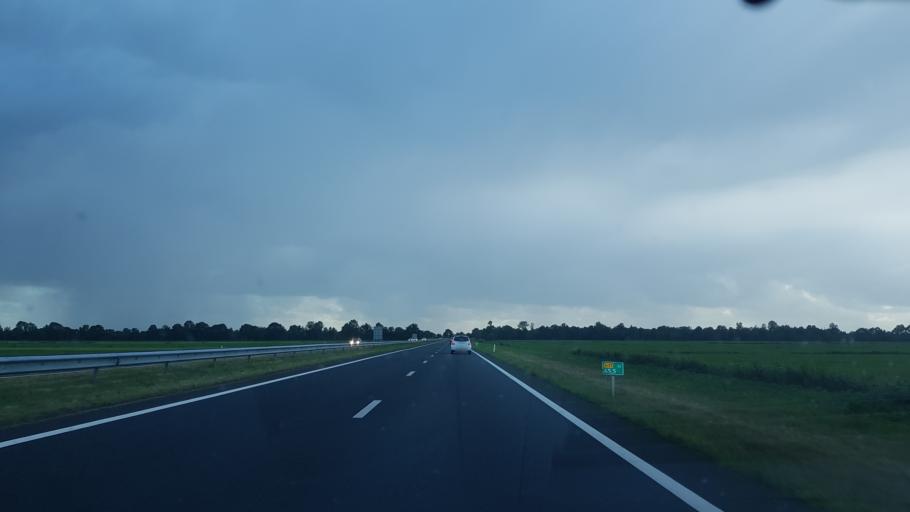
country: NL
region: Friesland
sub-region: Gemeente Smallingerland
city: Oudega
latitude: 53.1451
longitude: 6.0088
